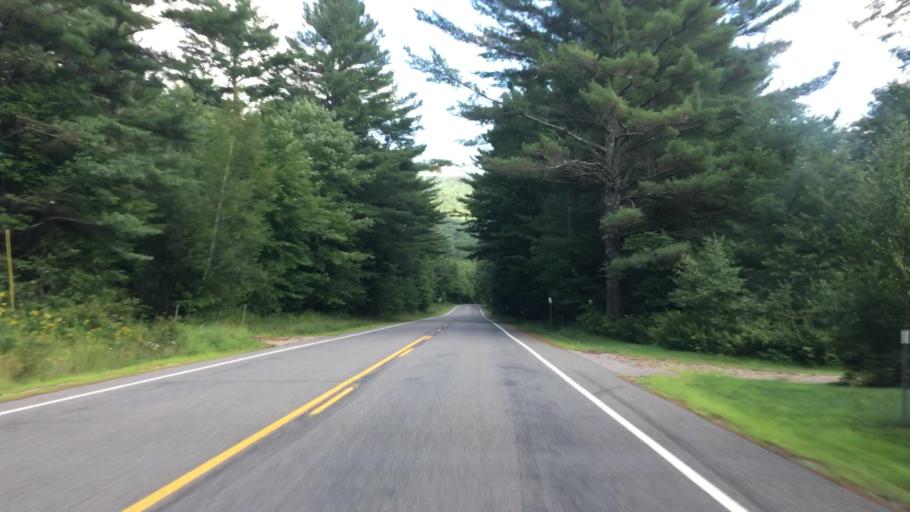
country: US
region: New Hampshire
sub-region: Grafton County
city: Woodstock
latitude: 44.0784
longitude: -71.8005
